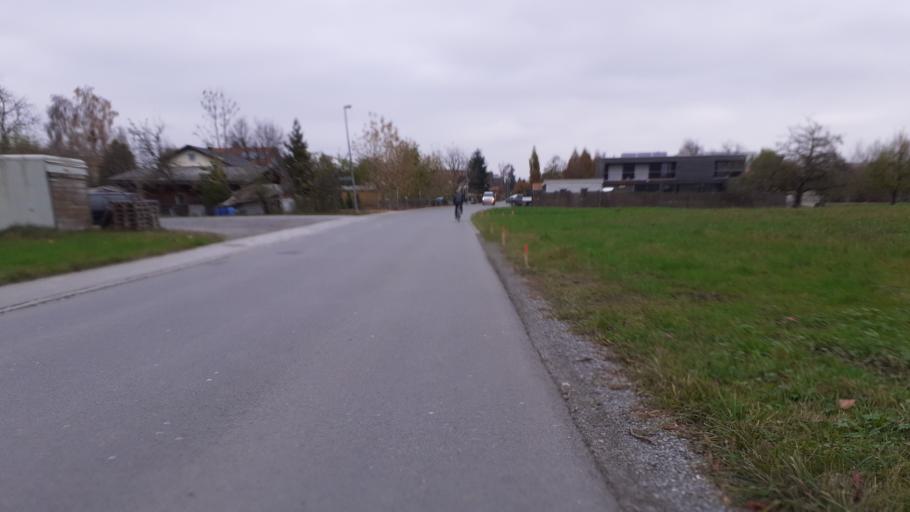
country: AT
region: Vorarlberg
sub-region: Politischer Bezirk Dornbirn
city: Lustenau
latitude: 47.4111
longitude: 9.6631
